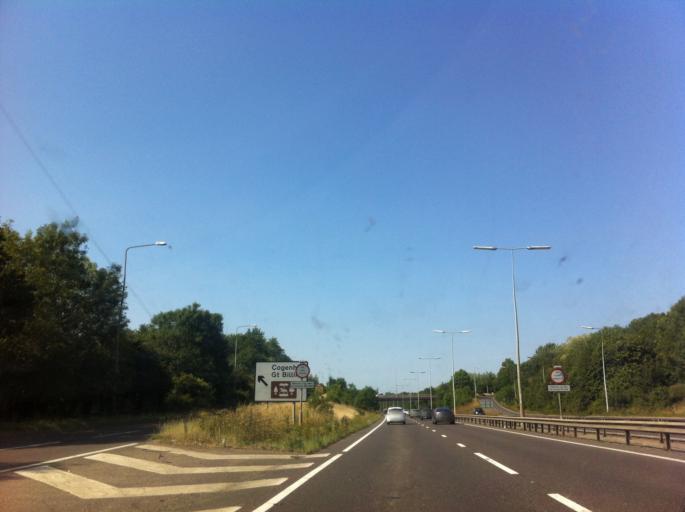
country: GB
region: England
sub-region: Northamptonshire
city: Earls Barton
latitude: 52.2528
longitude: -0.8029
